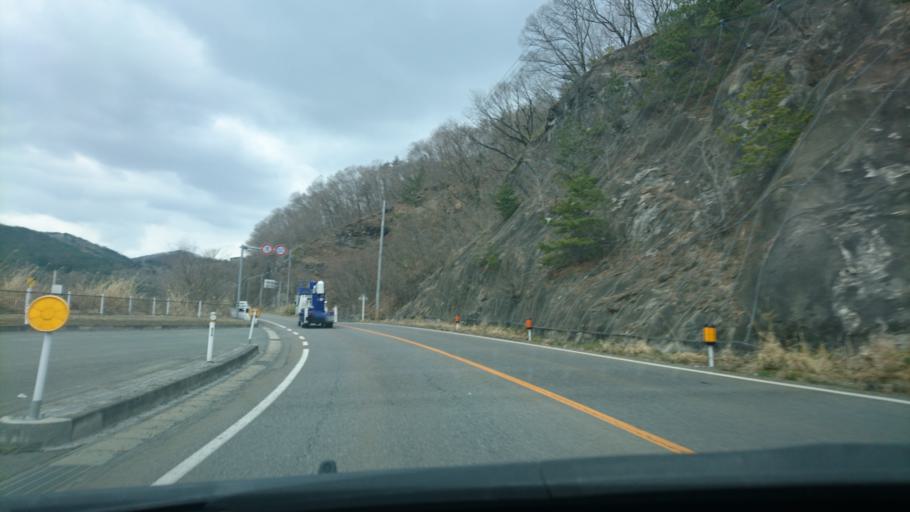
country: JP
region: Iwate
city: Hanamaki
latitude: 39.3578
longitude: 141.3235
